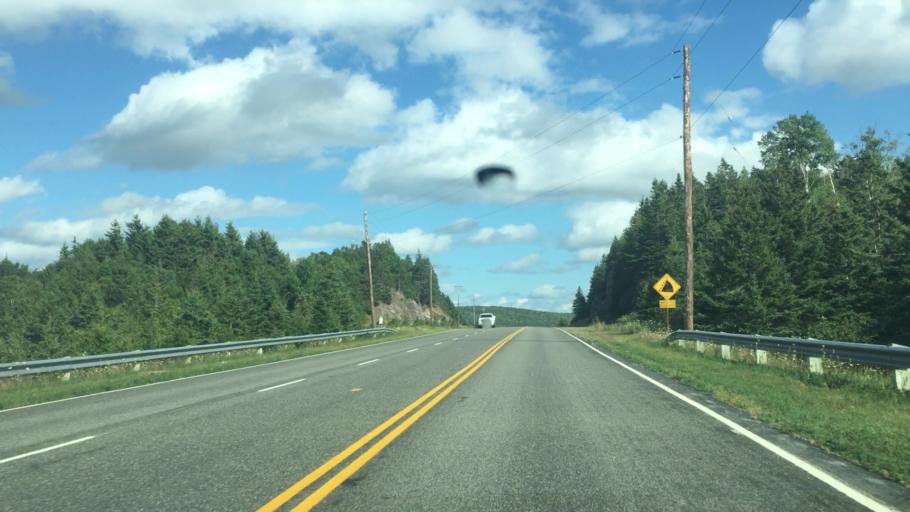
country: CA
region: Nova Scotia
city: Sydney
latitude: 45.8149
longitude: -60.6863
